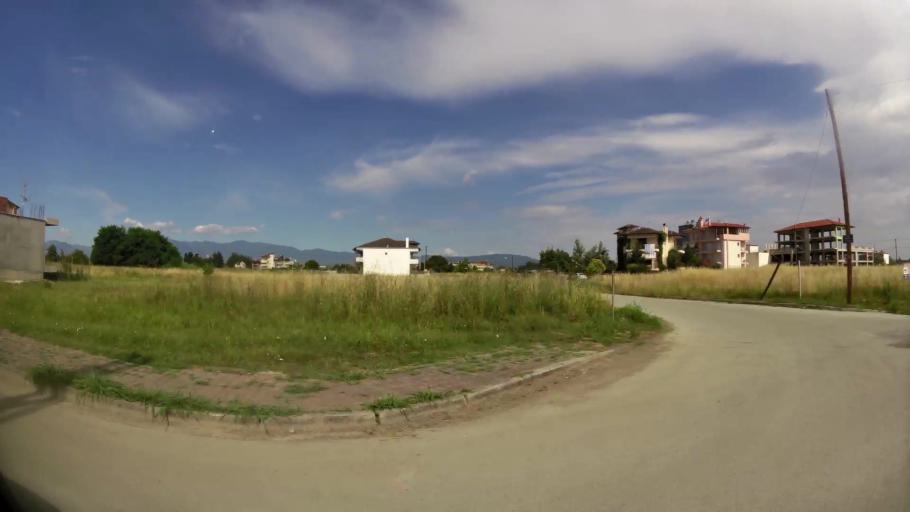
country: GR
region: Central Macedonia
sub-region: Nomos Pierias
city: Katerini
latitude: 40.2823
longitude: 22.5141
